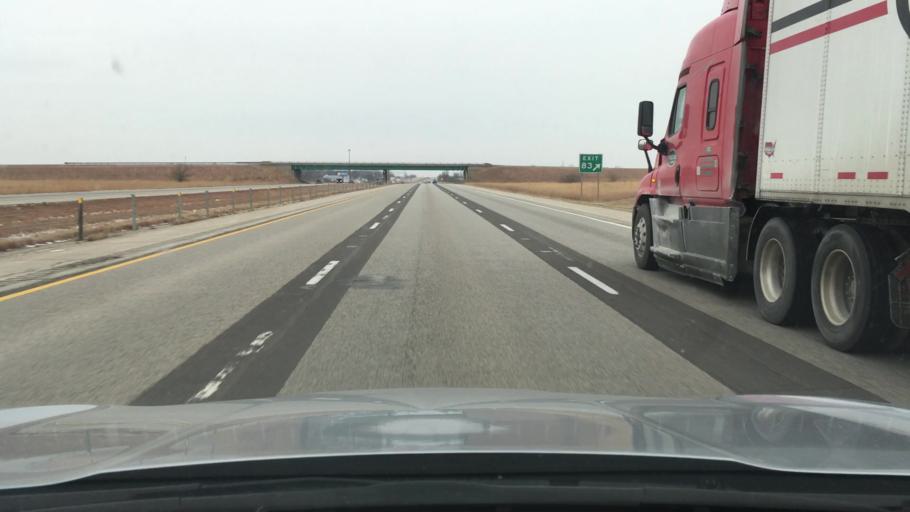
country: US
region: Illinois
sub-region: Sangamon County
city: Divernon
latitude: 39.6135
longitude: -89.6467
